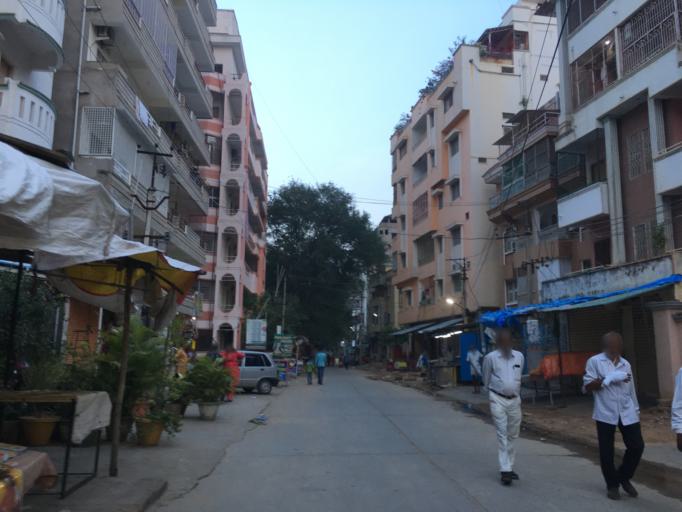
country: IN
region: Andhra Pradesh
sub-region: Anantapur
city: Puttaparthi
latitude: 14.1647
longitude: 77.8138
